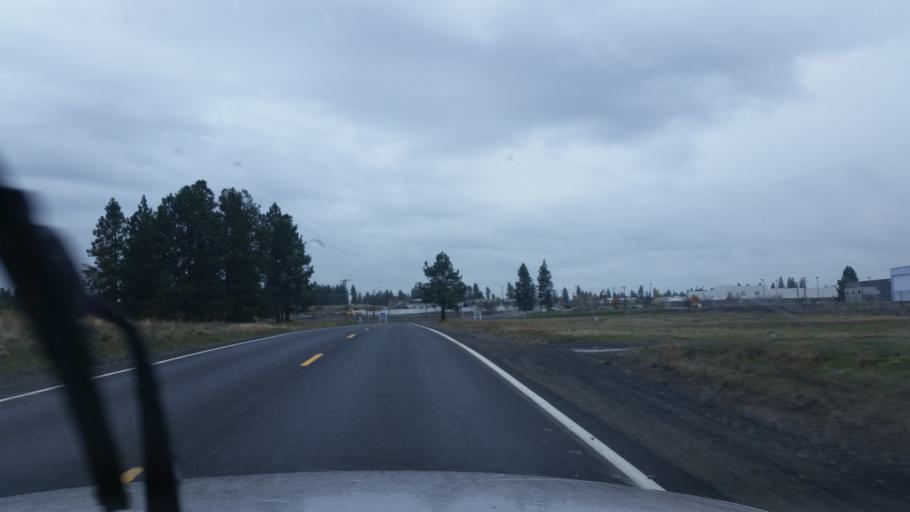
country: US
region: Washington
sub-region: Spokane County
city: Airway Heights
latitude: 47.6313
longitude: -117.5138
